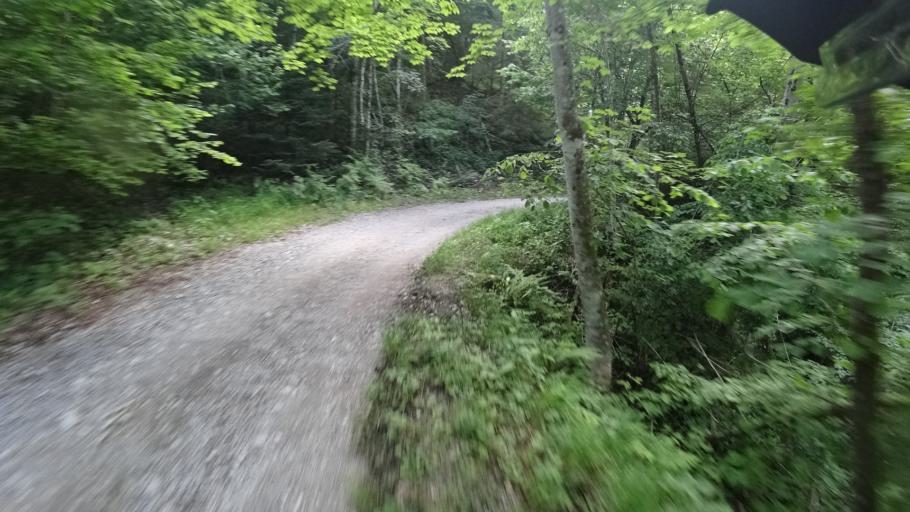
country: SI
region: Osilnica
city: Osilnica
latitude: 45.4633
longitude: 14.7058
